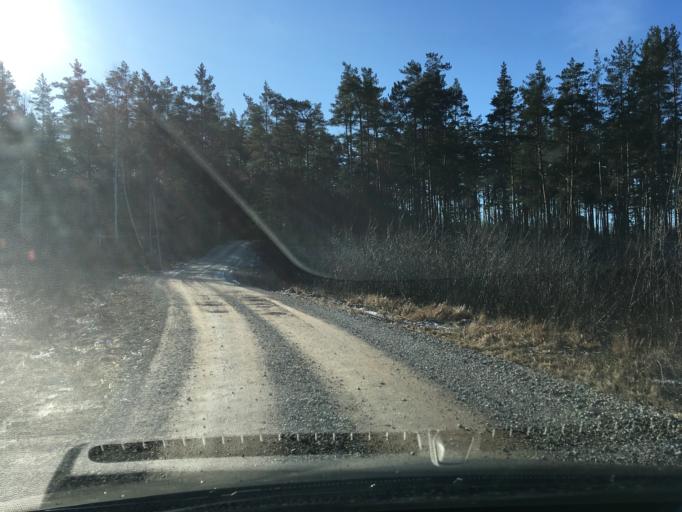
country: EE
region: Laeaene
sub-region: Lihula vald
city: Lihula
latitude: 58.5682
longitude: 23.6912
